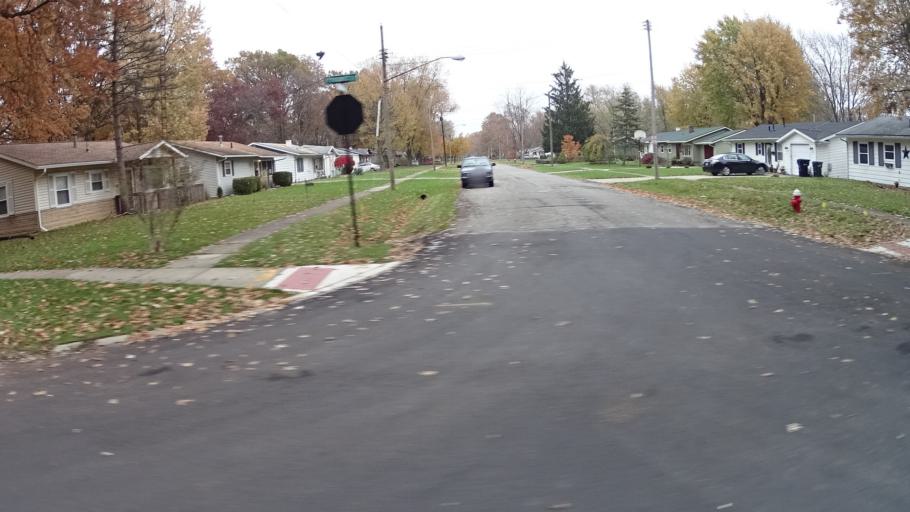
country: US
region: Ohio
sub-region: Lorain County
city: Elyria
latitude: 41.3604
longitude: -82.0886
